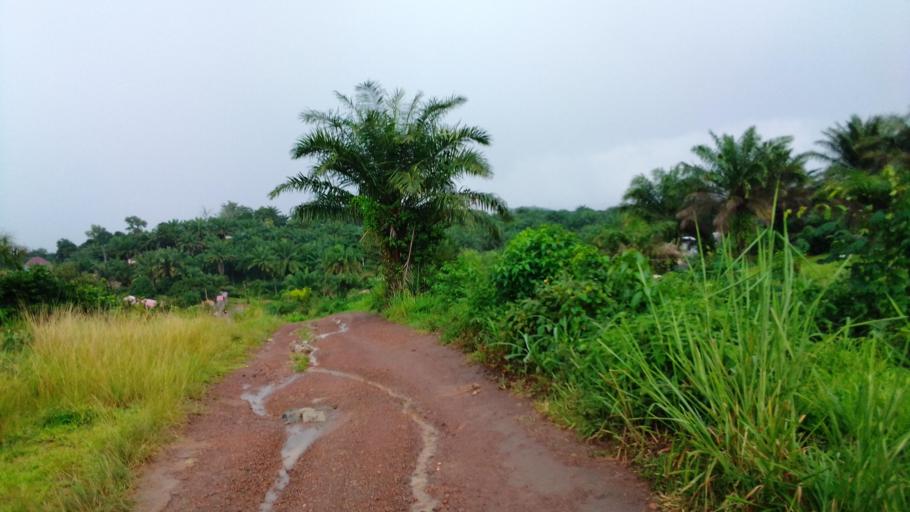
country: SL
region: Eastern Province
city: Kenema
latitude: 7.8798
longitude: -11.1736
